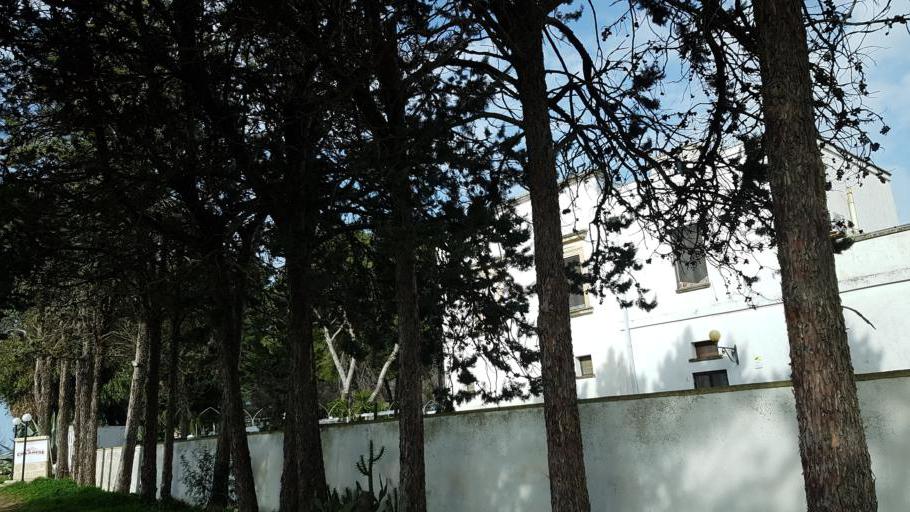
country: IT
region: Apulia
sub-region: Provincia di Brindisi
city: Brindisi
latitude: 40.6242
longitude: 17.8963
